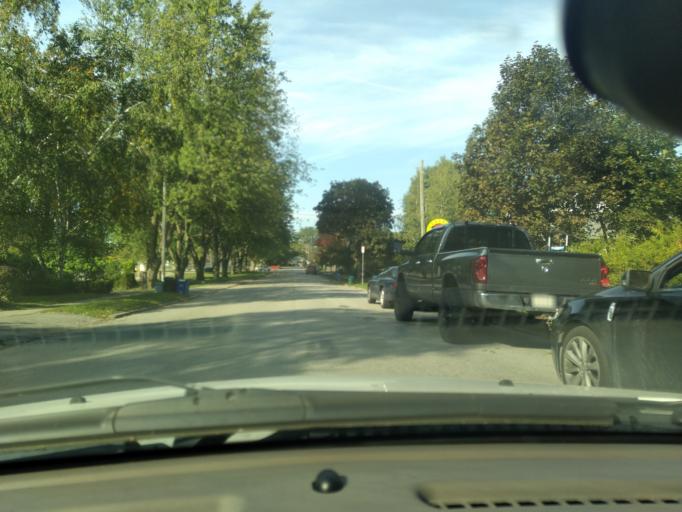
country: CA
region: Ontario
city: Barrie
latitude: 44.3699
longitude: -79.6894
